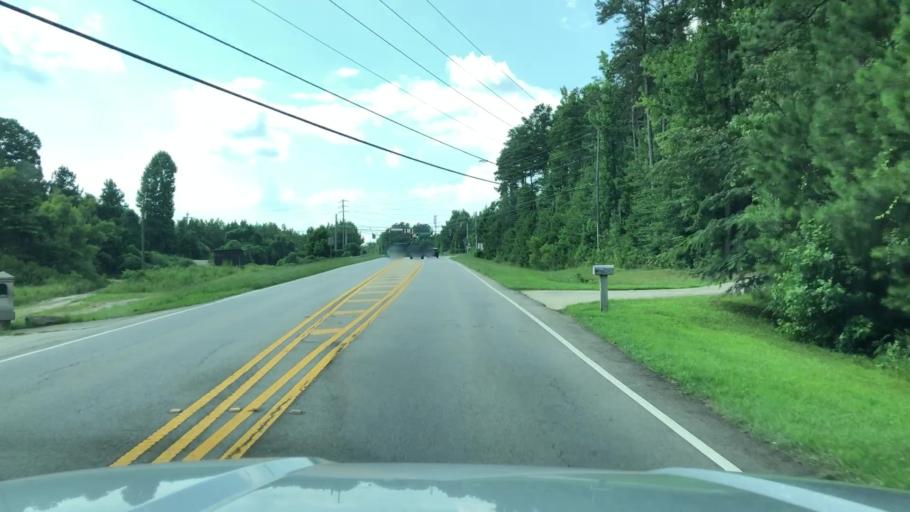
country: US
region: Georgia
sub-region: Paulding County
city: Hiram
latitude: 33.9416
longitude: -84.7645
